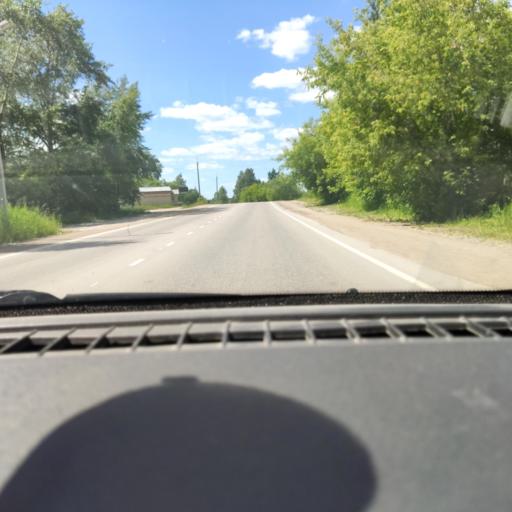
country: RU
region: Perm
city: Krasnokamsk
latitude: 58.0776
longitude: 55.7088
